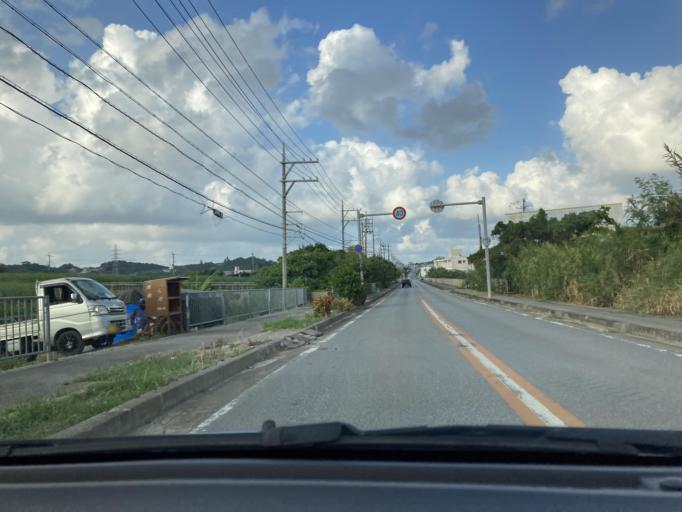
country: JP
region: Okinawa
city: Itoman
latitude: 26.1413
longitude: 127.7010
